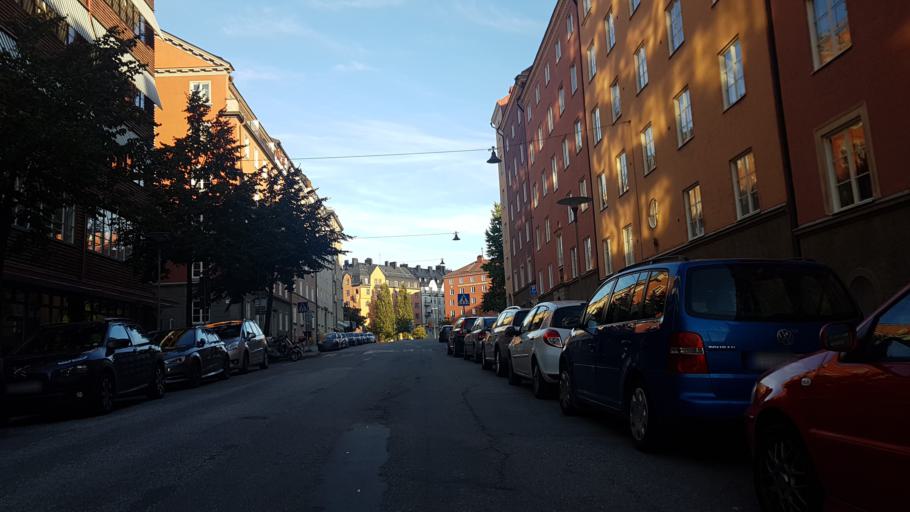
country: SE
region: Stockholm
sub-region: Stockholms Kommun
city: Stockholm
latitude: 59.3457
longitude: 18.0369
